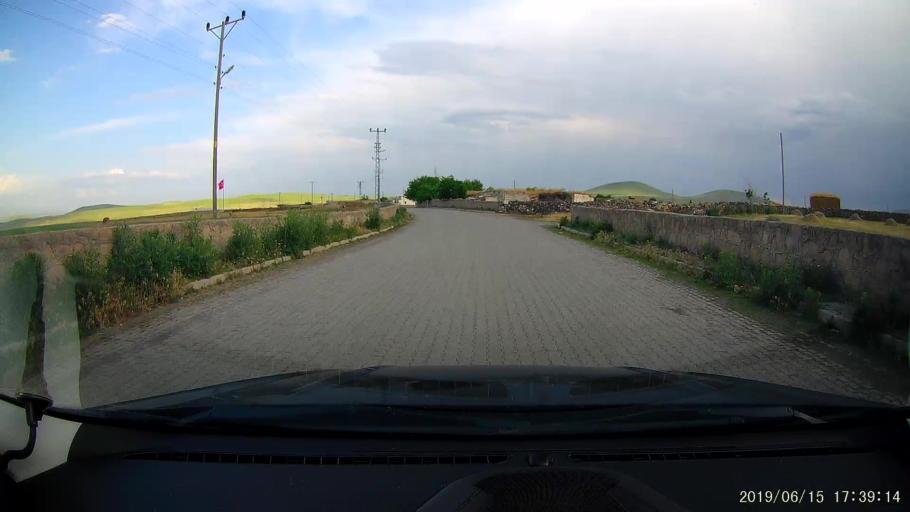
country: TR
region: Kars
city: Basgedikler
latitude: 40.5170
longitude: 43.5695
